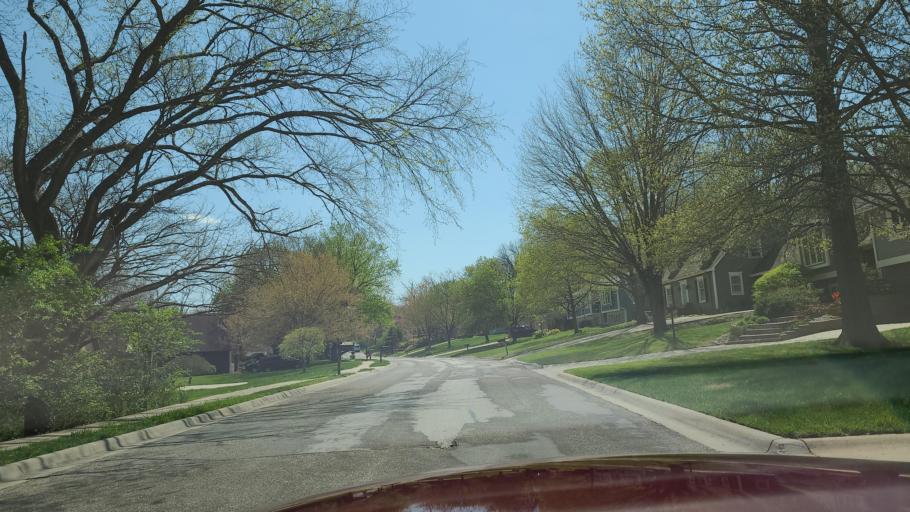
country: US
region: Kansas
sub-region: Douglas County
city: Lawrence
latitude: 38.9630
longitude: -95.2755
